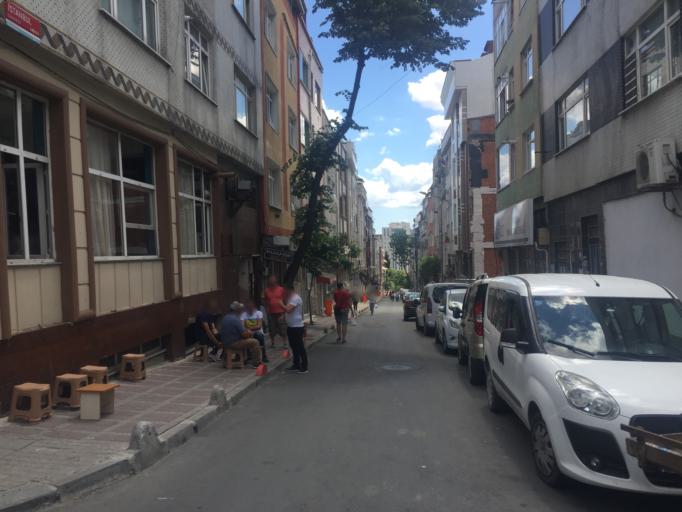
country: TR
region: Istanbul
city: Esenler
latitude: 41.0535
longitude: 28.9027
